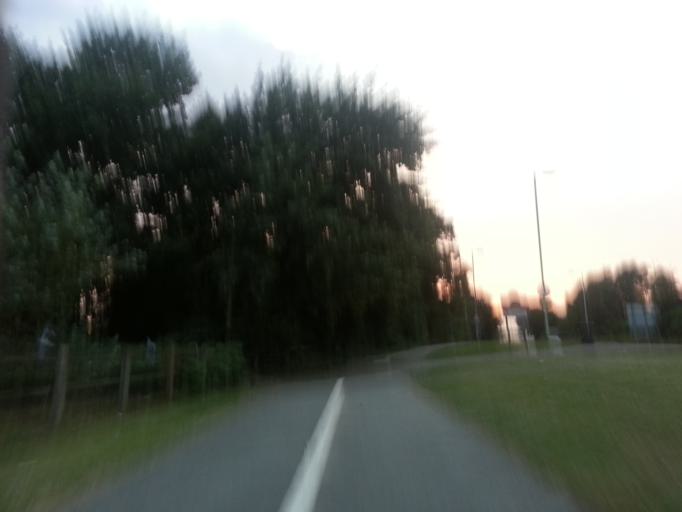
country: GB
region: England
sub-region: Suffolk
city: Kesgrave
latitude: 52.0261
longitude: 1.2069
